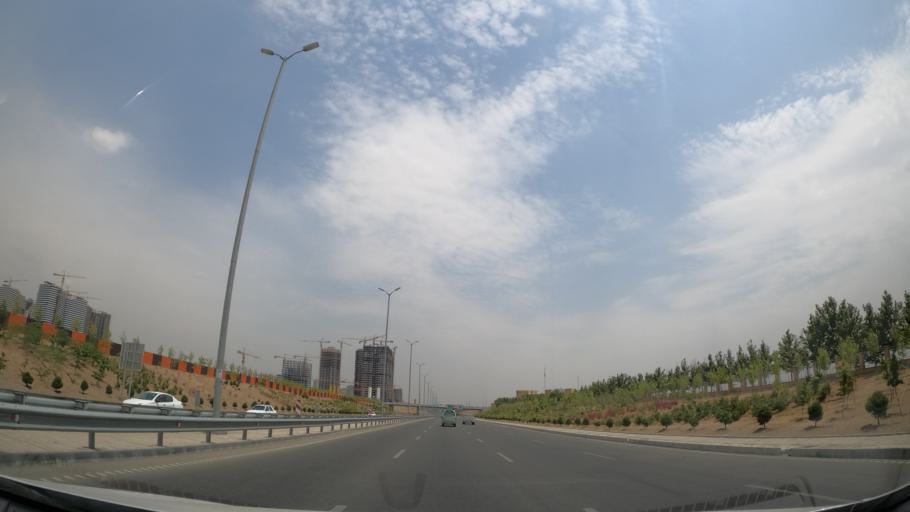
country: IR
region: Tehran
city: Shahr-e Qods
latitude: 35.7507
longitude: 51.1709
